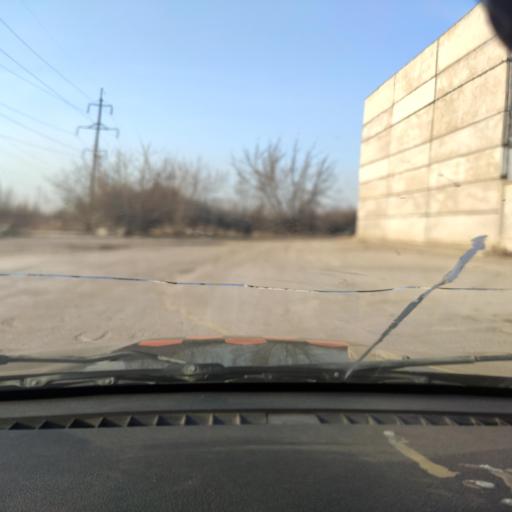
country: RU
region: Samara
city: Tol'yatti
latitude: 53.5837
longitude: 49.2715
